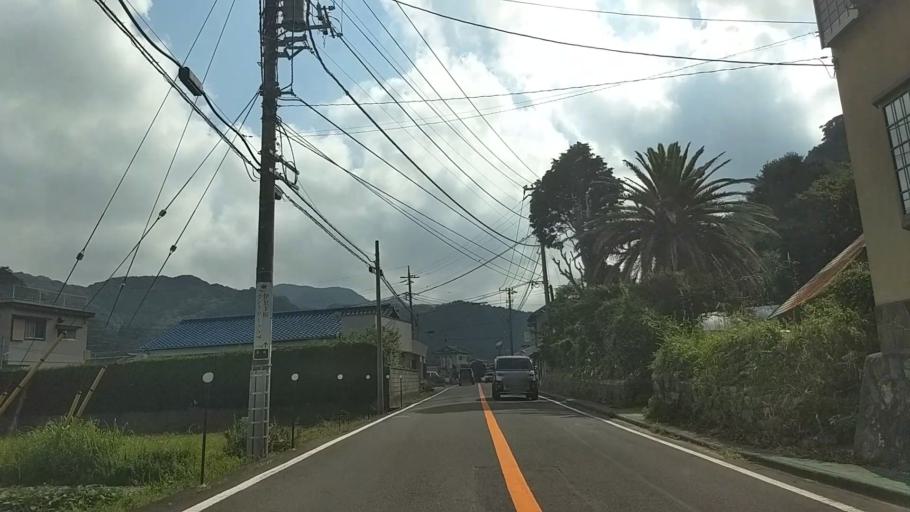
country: JP
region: Shizuoka
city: Shimoda
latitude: 34.6486
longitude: 138.8546
